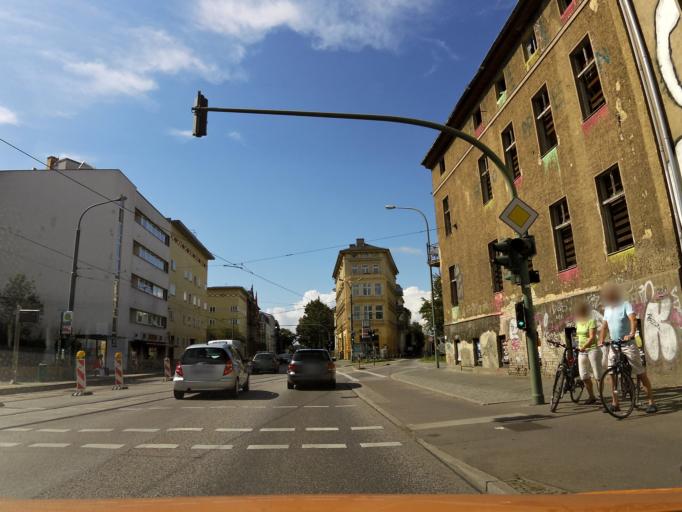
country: DE
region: Brandenburg
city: Potsdam
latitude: 52.3952
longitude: 13.0400
